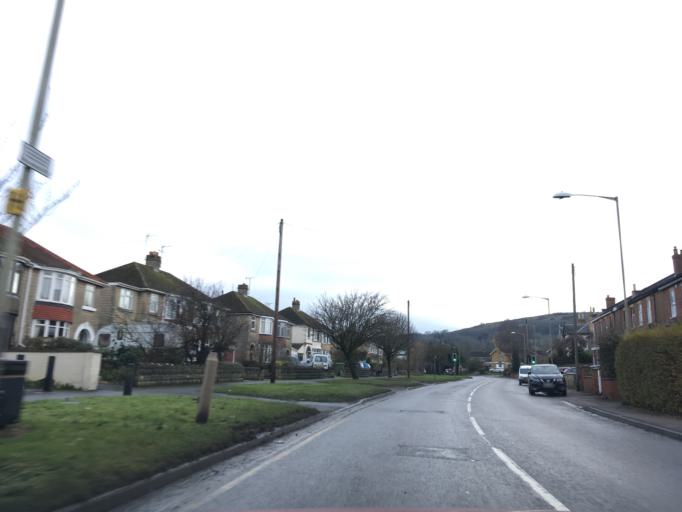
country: GB
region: England
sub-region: Gloucestershire
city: Charlton Kings
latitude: 51.8799
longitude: -2.0545
